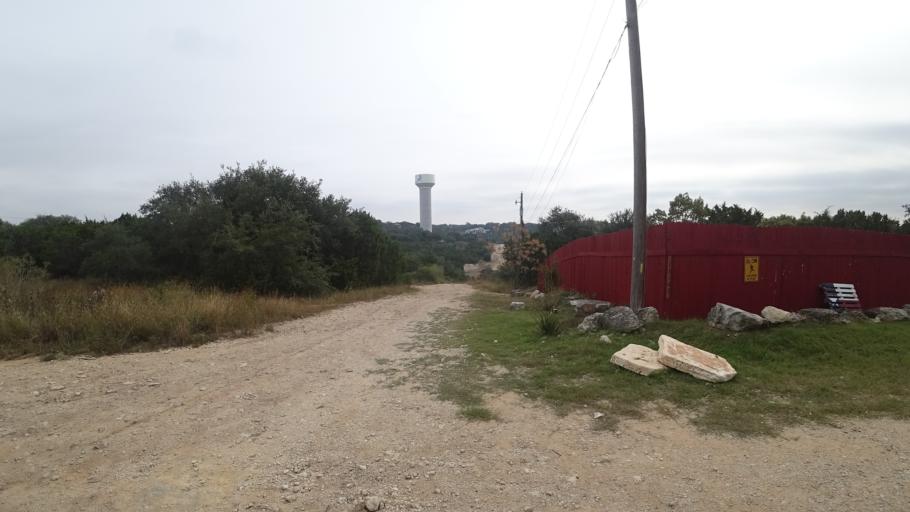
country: US
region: Texas
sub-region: Travis County
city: Hudson Bend
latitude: 30.3951
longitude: -97.9254
